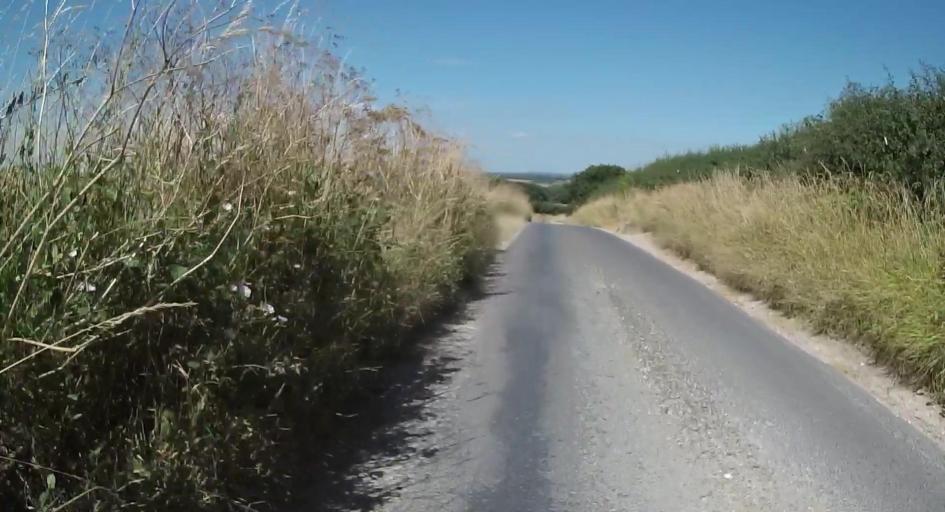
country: GB
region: England
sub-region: Dorset
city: Bovington Camp
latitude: 50.6606
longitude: -2.3029
